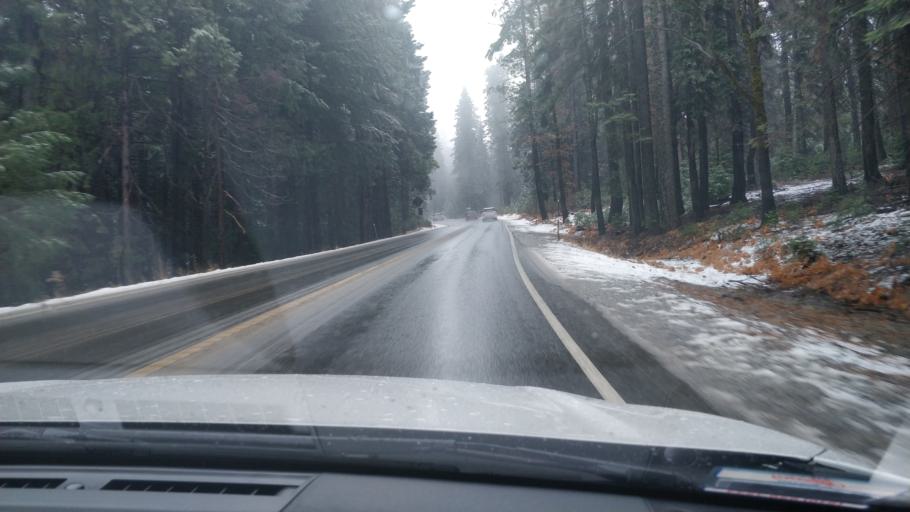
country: US
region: California
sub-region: Nevada County
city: Nevada City
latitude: 39.3096
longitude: -120.7668
